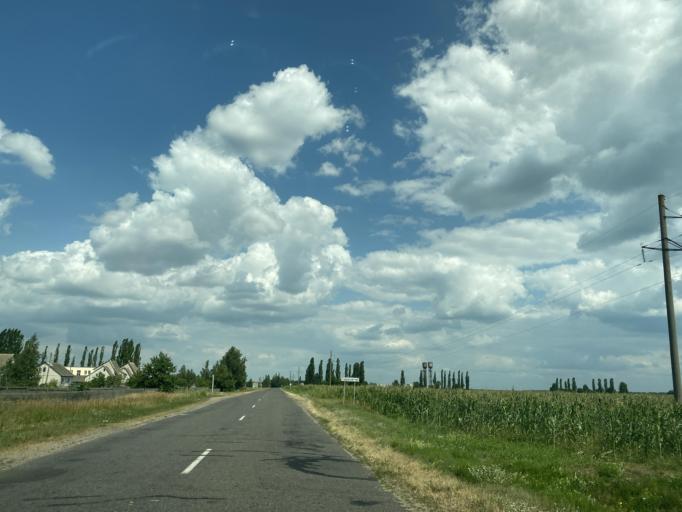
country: BY
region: Brest
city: Ivanava
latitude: 52.3428
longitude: 25.6261
